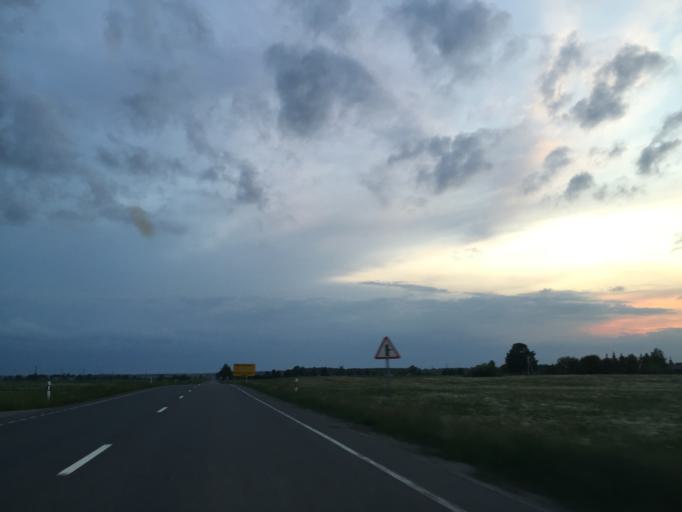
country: LT
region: Telsiu apskritis
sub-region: Telsiai
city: Telsiai
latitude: 56.0037
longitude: 22.3838
